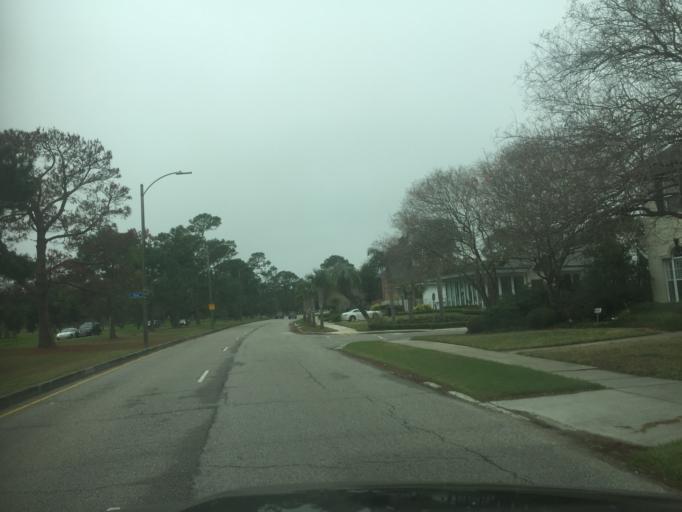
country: US
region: Louisiana
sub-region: Orleans Parish
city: New Orleans
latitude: 30.0186
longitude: -90.0917
